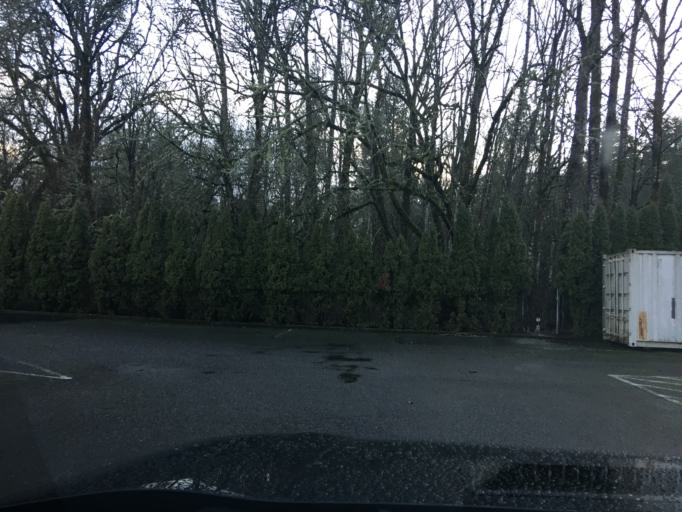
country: US
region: Oregon
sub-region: Washington County
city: Aloha
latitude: 45.5034
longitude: -122.8489
